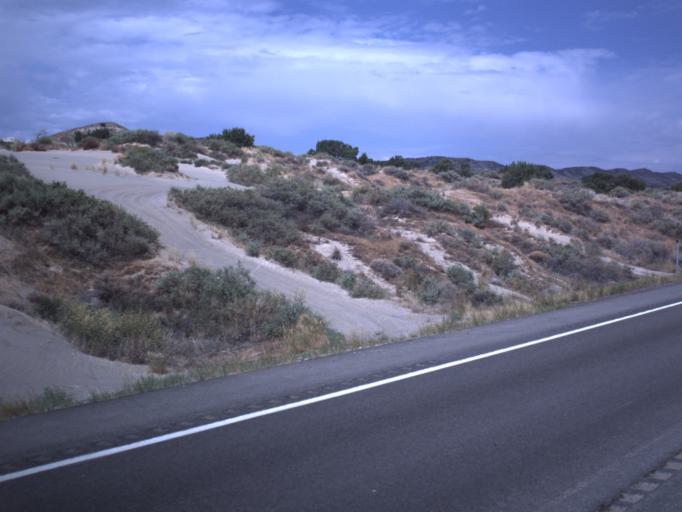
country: US
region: Utah
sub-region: Uintah County
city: Naples
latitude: 40.3506
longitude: -109.4914
